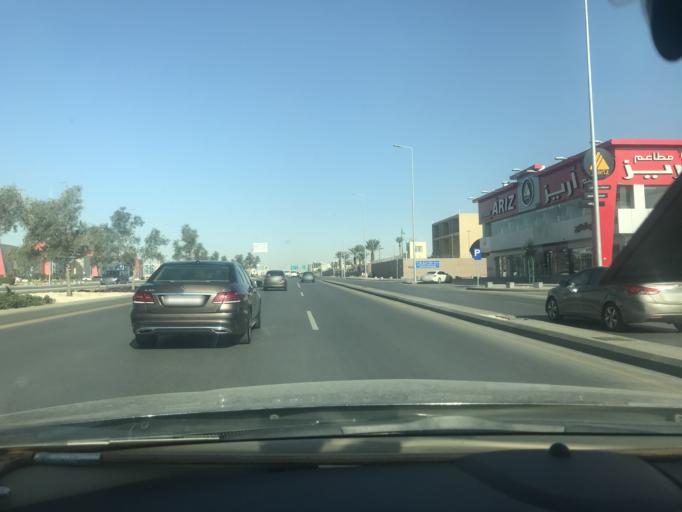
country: SA
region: Ar Riyad
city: Riyadh
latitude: 24.7411
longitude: 46.6831
